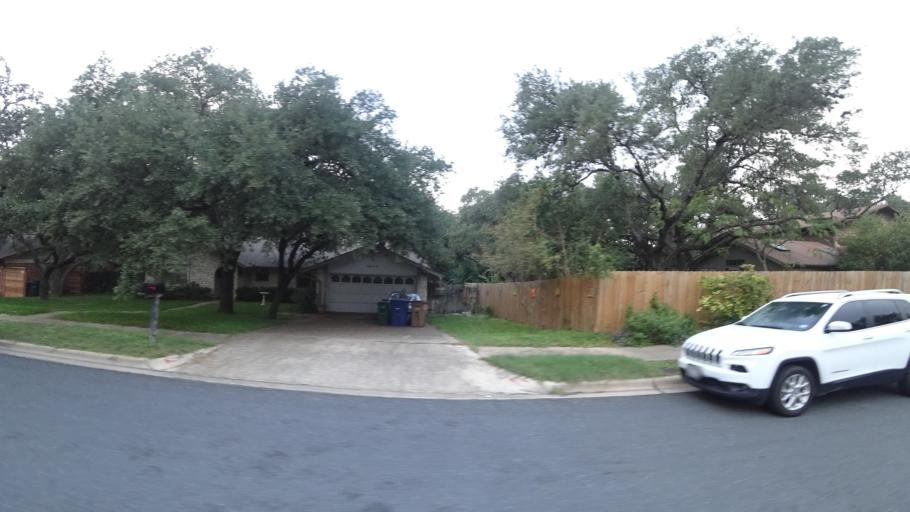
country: US
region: Texas
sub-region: Travis County
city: Austin
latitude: 30.3446
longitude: -97.6940
